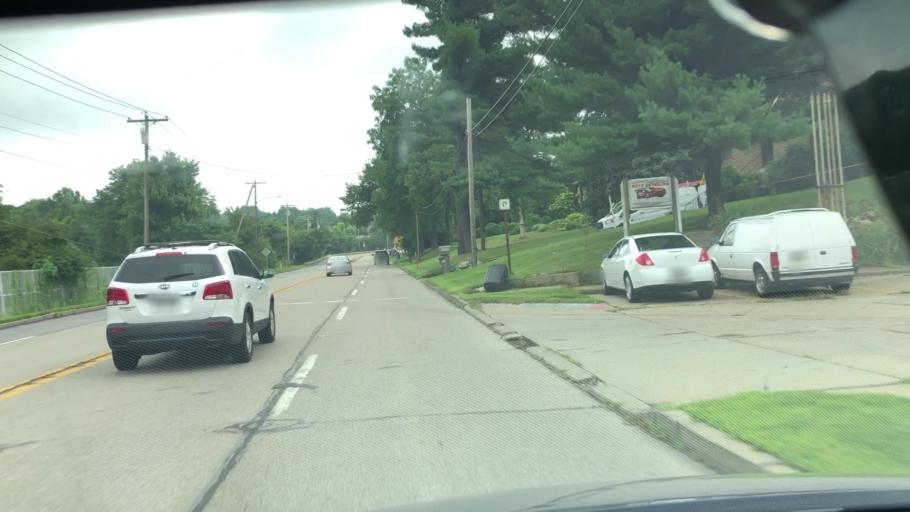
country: US
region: Pennsylvania
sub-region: Allegheny County
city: Upper Saint Clair
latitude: 40.3359
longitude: -80.0677
